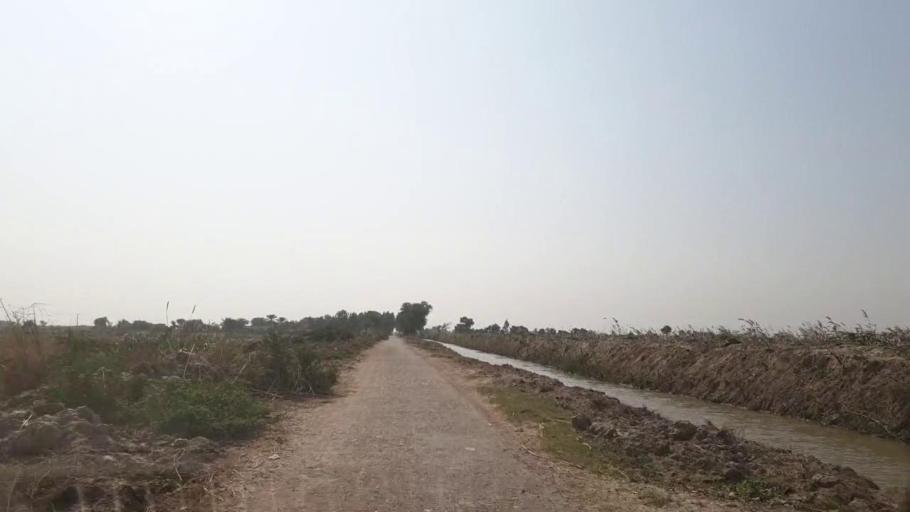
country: PK
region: Sindh
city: Bulri
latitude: 24.9675
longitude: 68.3946
